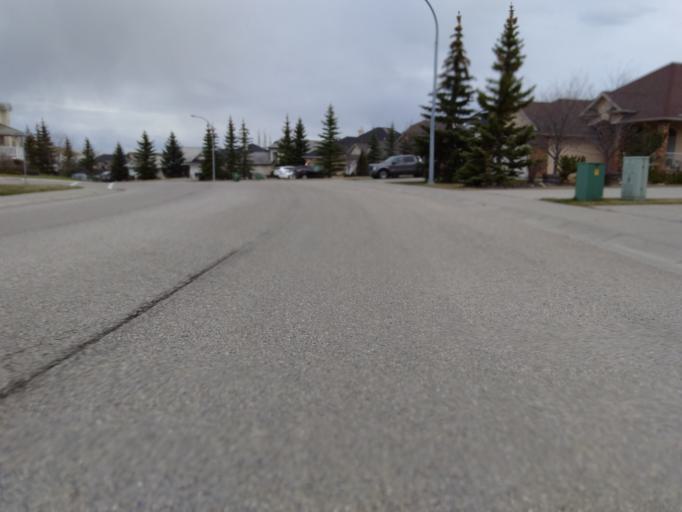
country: CA
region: Alberta
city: Cochrane
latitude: 51.1843
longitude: -114.4261
